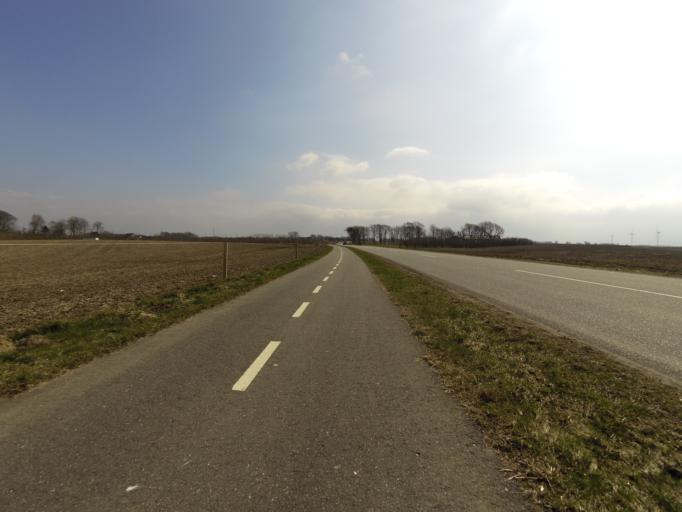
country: DK
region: Central Jutland
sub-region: Struer Kommune
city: Struer
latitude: 56.4483
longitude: 8.6227
